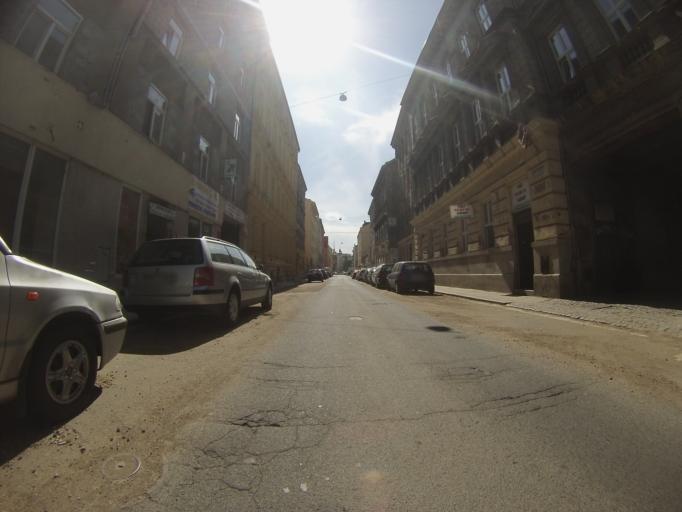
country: CZ
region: South Moravian
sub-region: Mesto Brno
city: Brno
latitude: 49.1994
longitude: 16.6201
